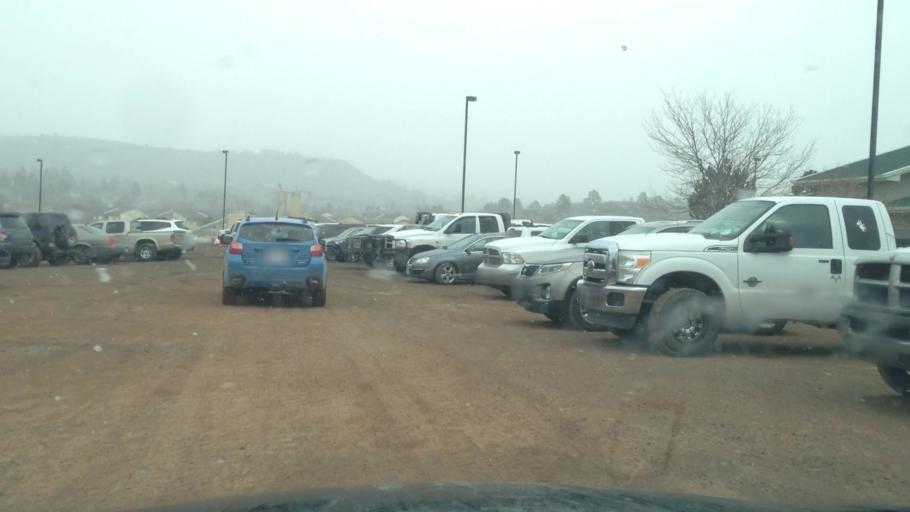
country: US
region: Colorado
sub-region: Douglas County
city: Castle Rock
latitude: 39.3646
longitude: -104.8546
